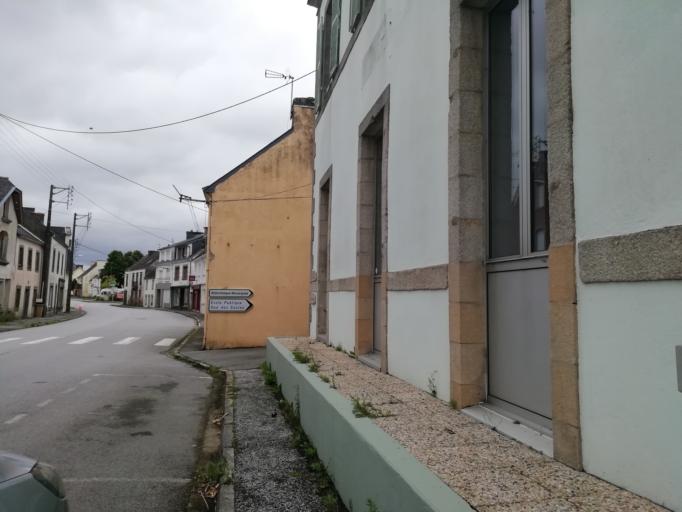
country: FR
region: Brittany
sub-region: Departement du Finistere
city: Spezet
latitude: 48.1264
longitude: -3.7196
